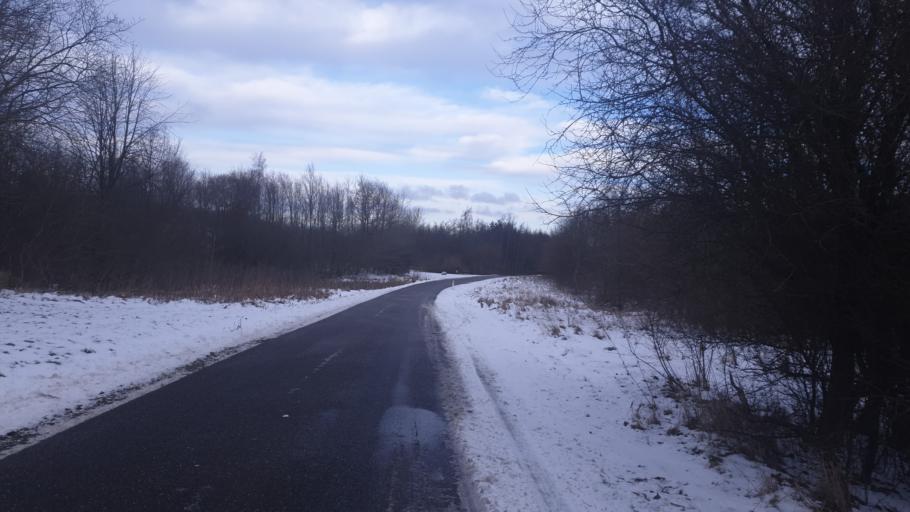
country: DK
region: Central Jutland
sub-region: Hedensted Kommune
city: Hedensted
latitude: 55.7924
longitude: 9.7306
